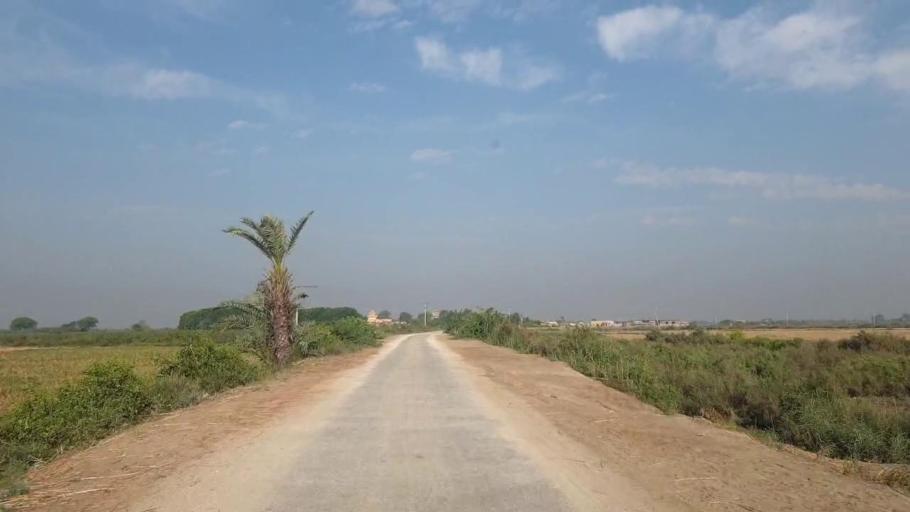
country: PK
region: Sindh
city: Tando Bago
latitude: 24.8546
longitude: 68.9677
